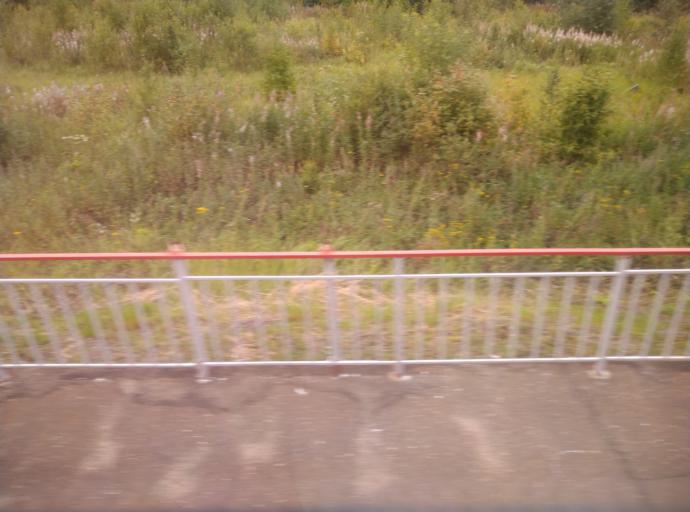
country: RU
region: Jaroslavl
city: Burmakino
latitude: 57.4371
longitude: 40.3754
